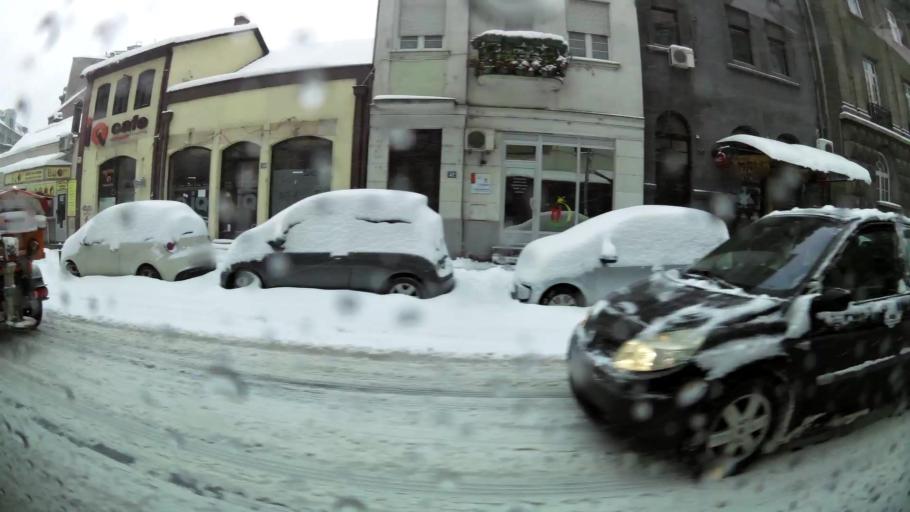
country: RS
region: Central Serbia
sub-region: Belgrade
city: Stari Grad
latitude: 44.8108
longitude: 20.4596
